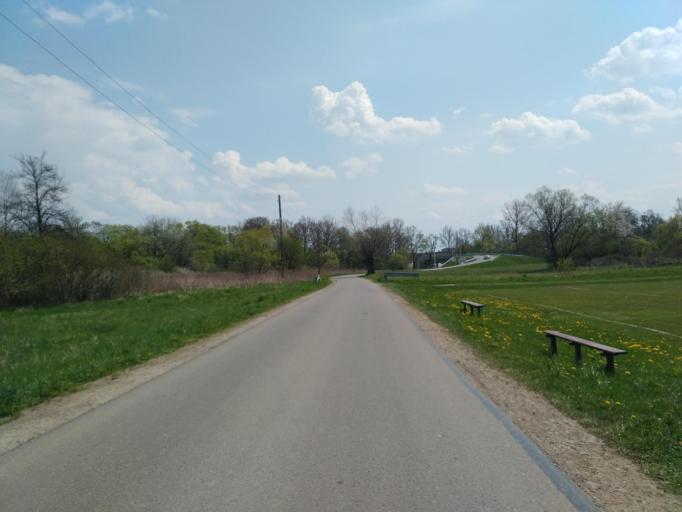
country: PL
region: Subcarpathian Voivodeship
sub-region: Powiat krosnienski
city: Jedlicze
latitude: 49.7296
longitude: 21.6194
